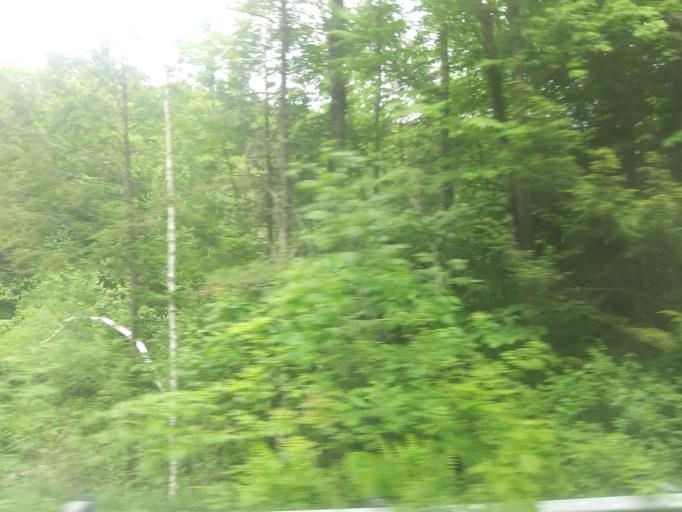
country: US
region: Massachusetts
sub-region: Franklin County
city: Buckland
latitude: 42.5664
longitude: -72.8078
